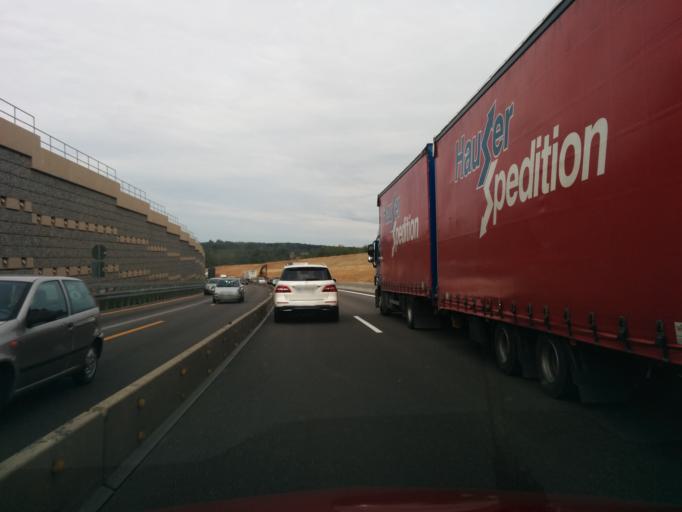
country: DE
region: Baden-Wuerttemberg
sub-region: Karlsruhe Region
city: Konigsbach-Stein
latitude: 48.9371
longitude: 8.5406
